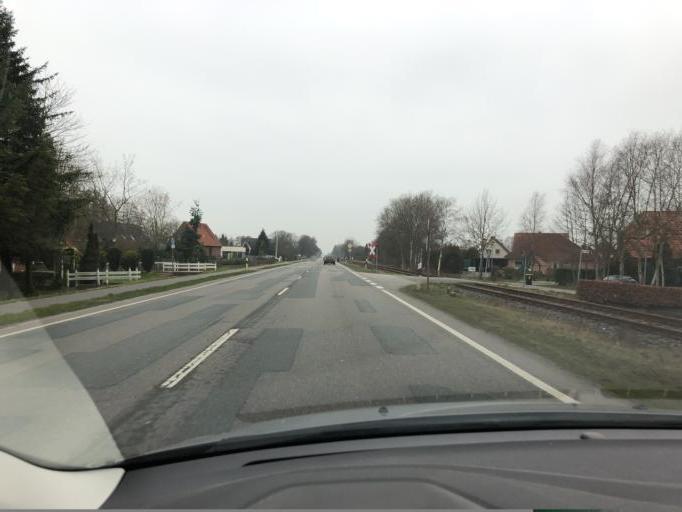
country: DE
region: Lower Saxony
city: Rechtsupweg
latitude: 53.4789
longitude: 7.3860
